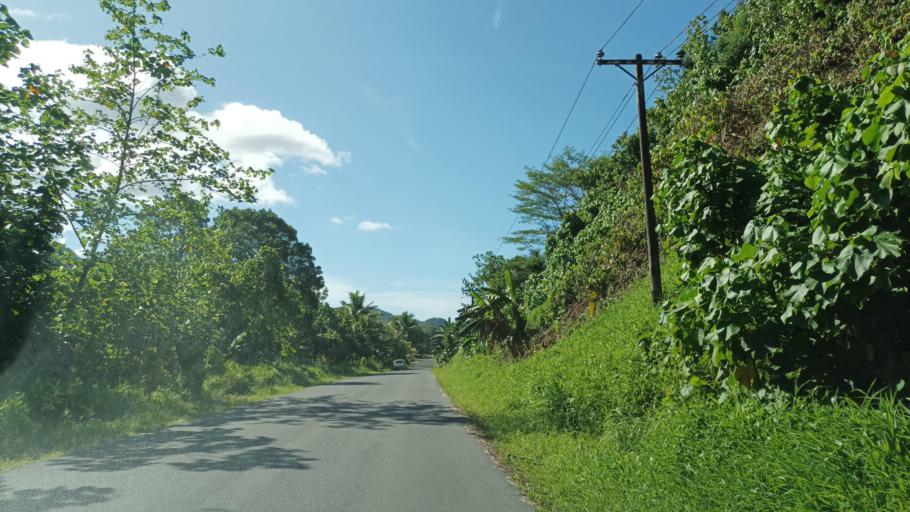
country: FM
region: Pohnpei
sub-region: Madolenihm Municipality
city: Madolenihm Municipality Government
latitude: 6.9156
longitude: 158.2911
